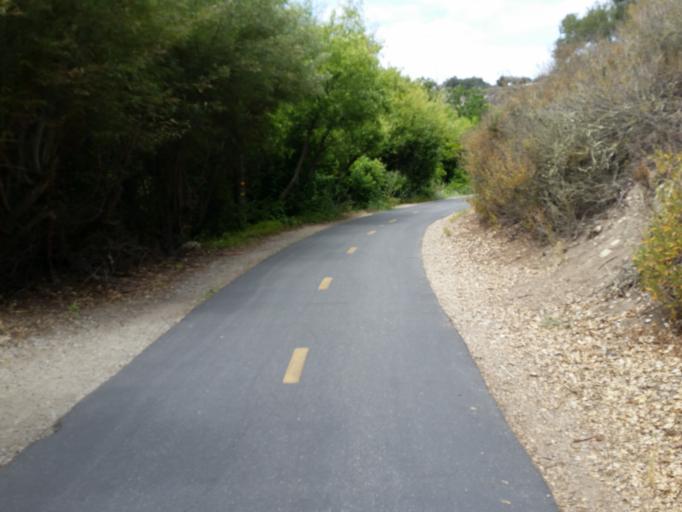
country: US
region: California
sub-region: San Luis Obispo County
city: Avila Beach
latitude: 35.1852
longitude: -120.7067
